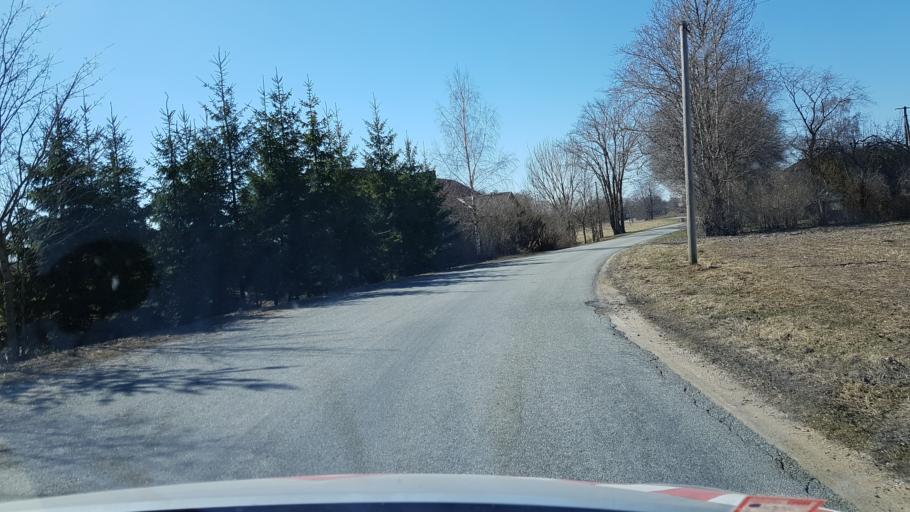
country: EE
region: Laeaene-Virumaa
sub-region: Rakke vald
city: Rakke
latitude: 59.0509
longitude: 26.4218
